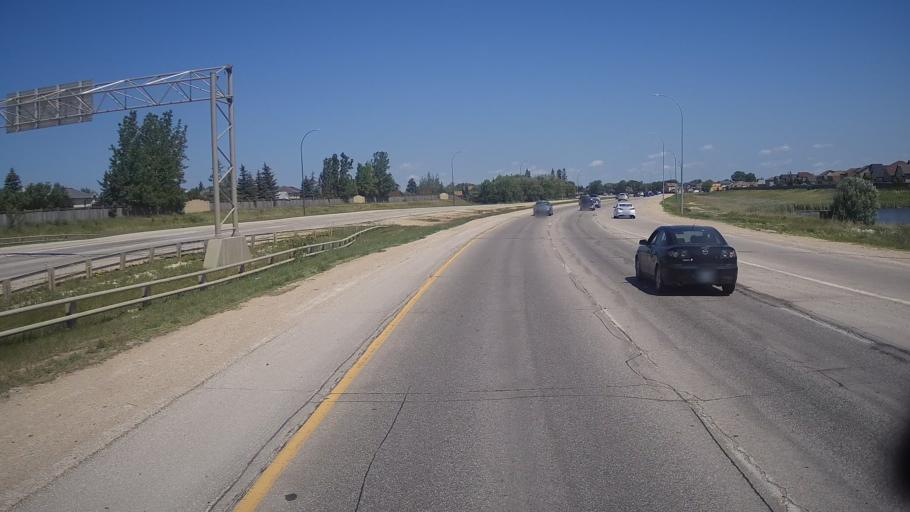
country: CA
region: Manitoba
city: Winnipeg
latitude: 49.9145
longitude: -97.0539
